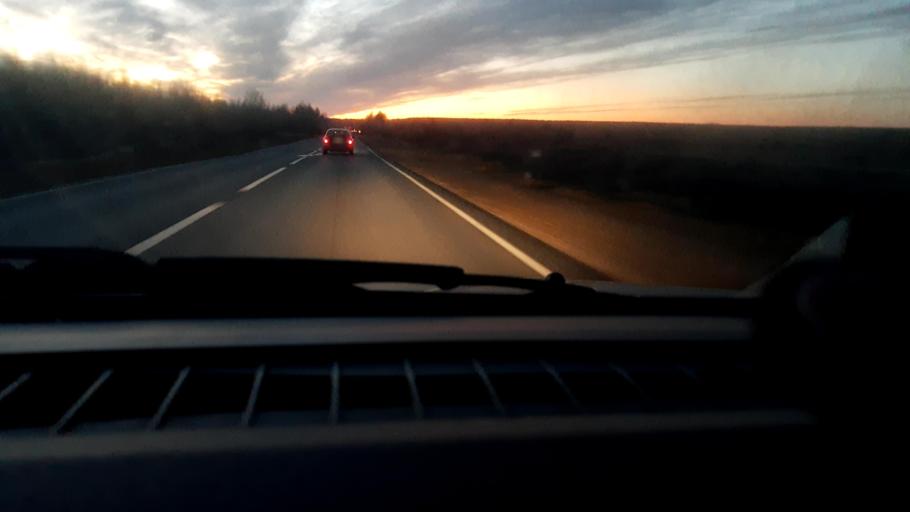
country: RU
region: Nizjnij Novgorod
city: Sukhobezvodnoye
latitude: 56.8601
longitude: 44.8645
